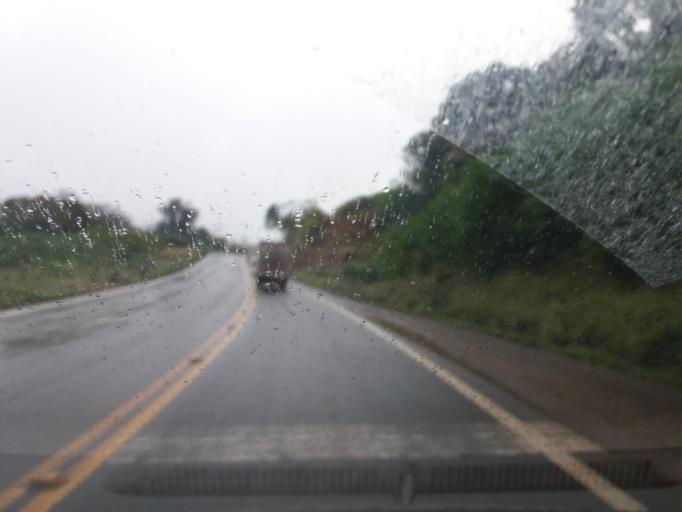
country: BR
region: Parana
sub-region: Realeza
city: Realeza
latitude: -25.4810
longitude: -53.5909
